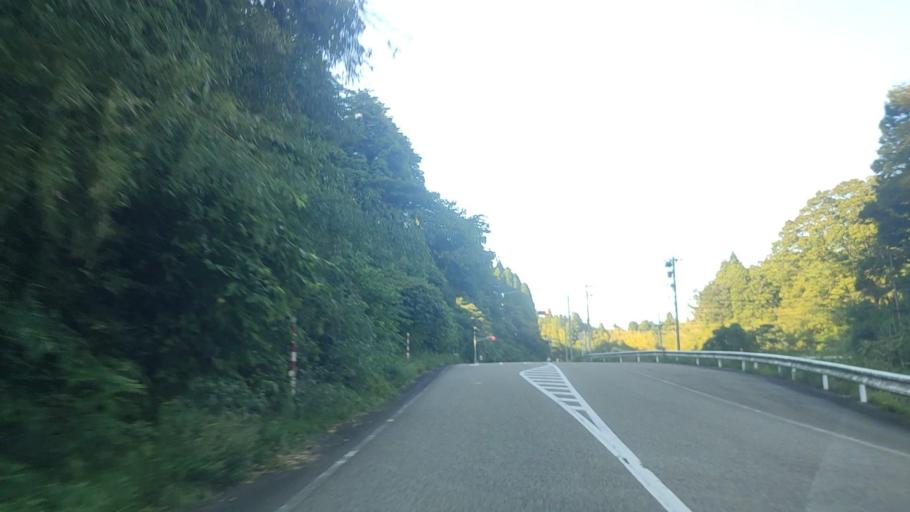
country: JP
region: Ishikawa
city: Nanao
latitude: 37.1170
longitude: 136.9651
